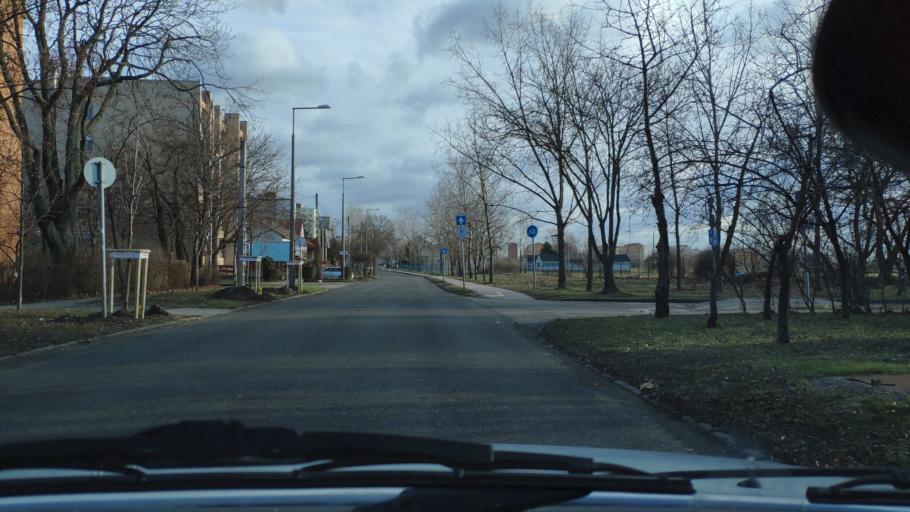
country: HU
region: Budapest
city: Budapest X. keruelet
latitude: 47.4774
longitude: 19.1533
